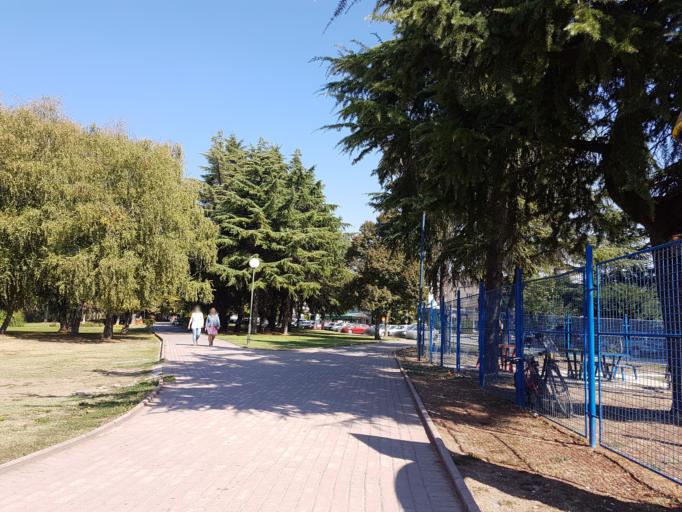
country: MK
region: Ohrid
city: Ohrid
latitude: 41.1046
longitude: 20.8080
